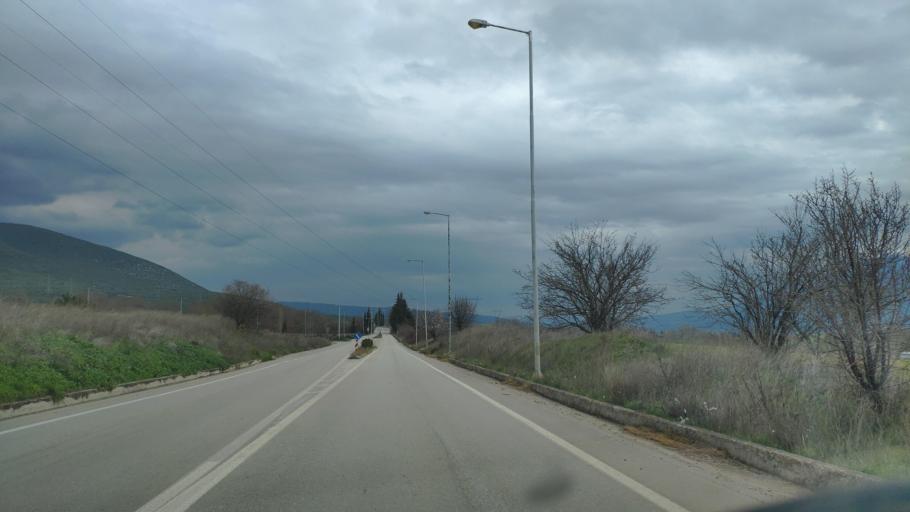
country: GR
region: Central Greece
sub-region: Nomos Fthiotidos
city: Amfikleia
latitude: 38.7092
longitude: 22.4867
